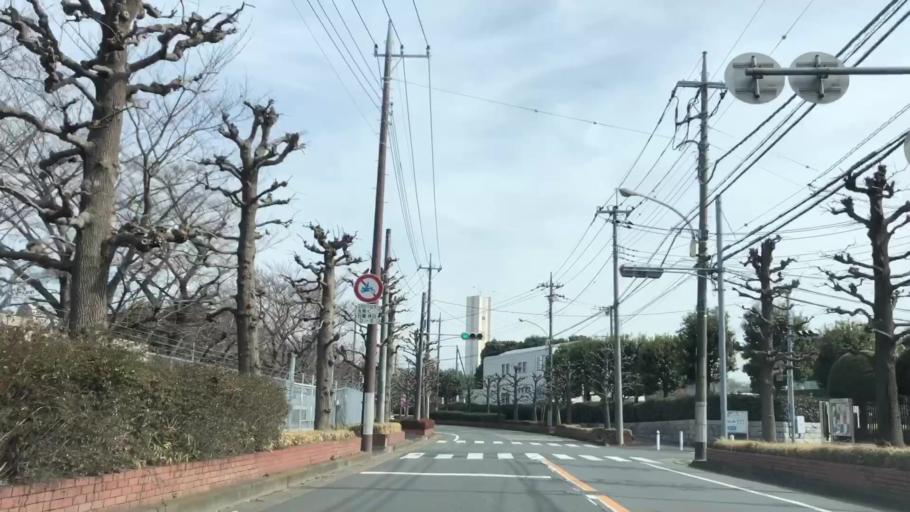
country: JP
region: Saitama
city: Wako
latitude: 35.7752
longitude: 139.6130
